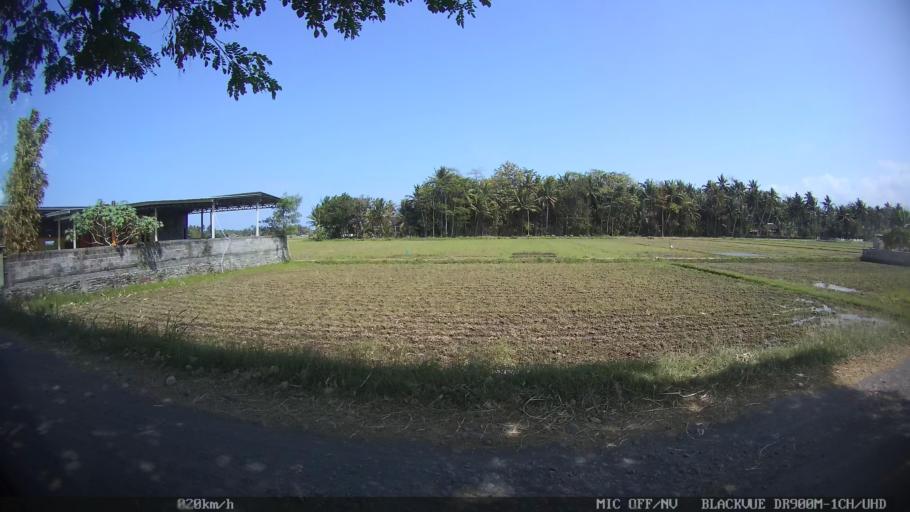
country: ID
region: Daerah Istimewa Yogyakarta
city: Srandakan
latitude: -7.9605
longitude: 110.2153
